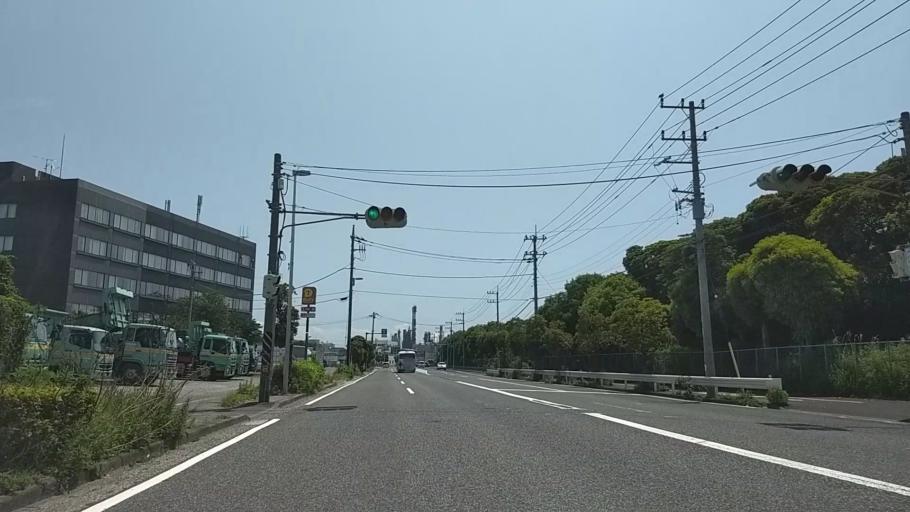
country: JP
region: Kanagawa
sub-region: Kawasaki-shi
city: Kawasaki
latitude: 35.5192
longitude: 139.7341
